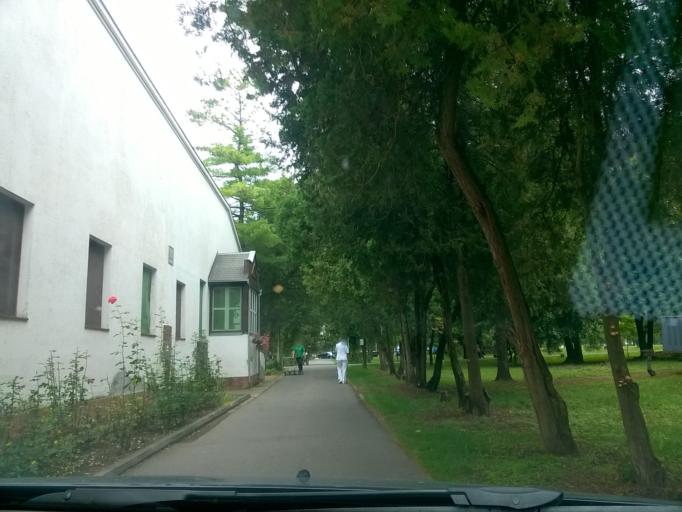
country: RS
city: Melenci
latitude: 45.5271
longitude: 20.3038
